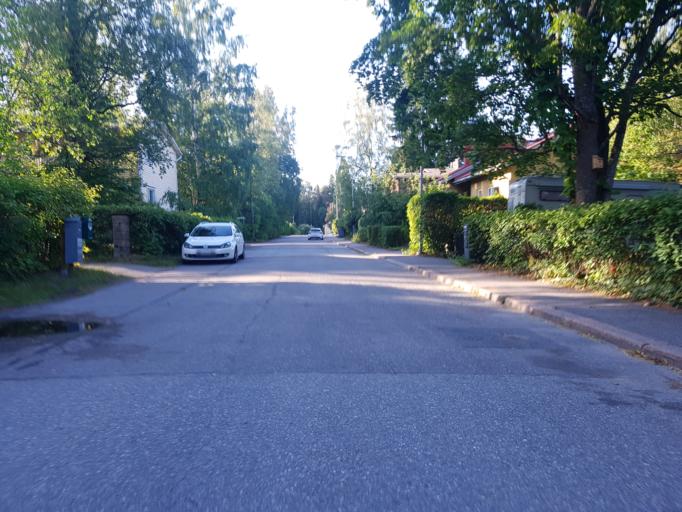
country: FI
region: Uusimaa
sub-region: Helsinki
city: Helsinki
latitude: 60.2427
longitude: 24.9190
